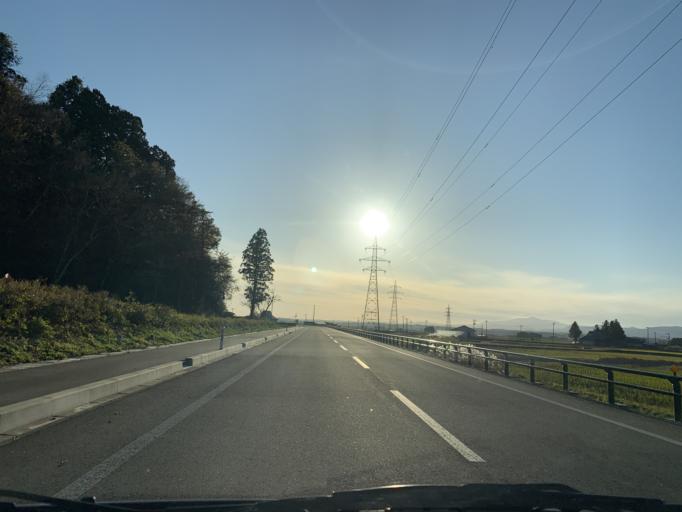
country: JP
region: Iwate
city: Mizusawa
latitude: 39.0718
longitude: 141.1862
